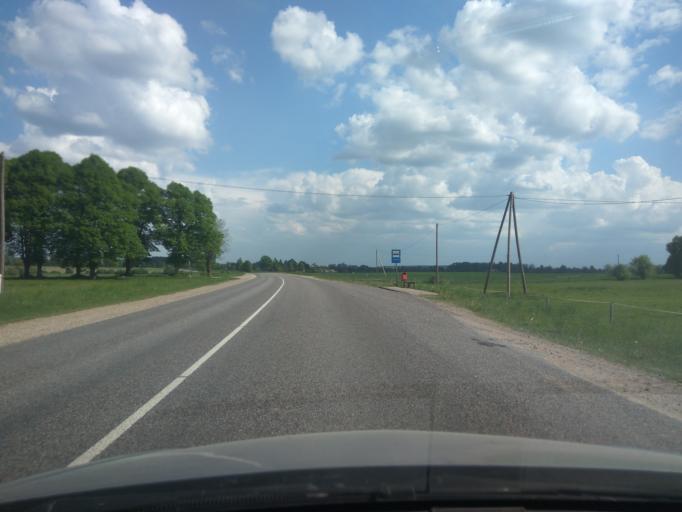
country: LV
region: Kuldigas Rajons
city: Kuldiga
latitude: 57.0113
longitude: 21.8799
